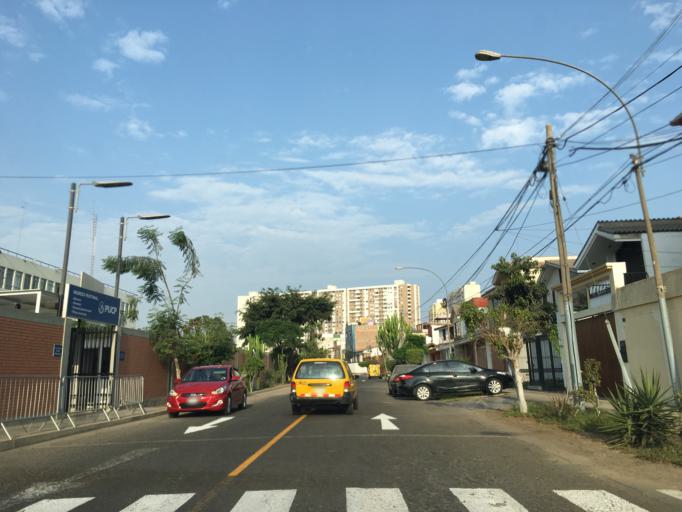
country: PE
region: Callao
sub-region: Callao
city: Callao
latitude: -12.0734
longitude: -77.0825
